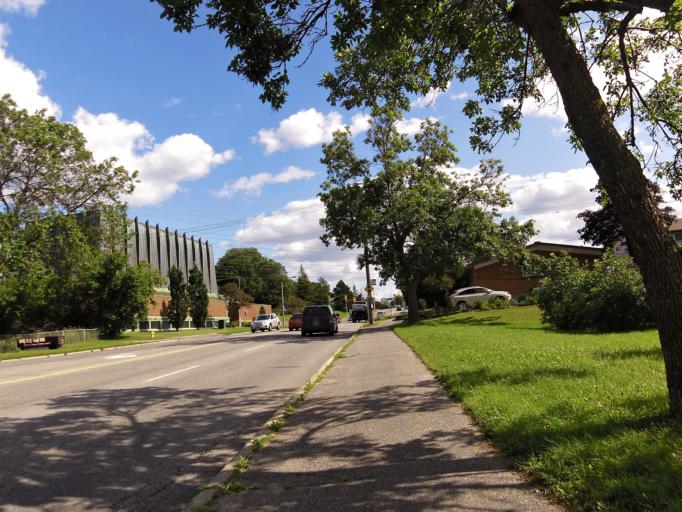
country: CA
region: Ontario
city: Ottawa
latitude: 45.3670
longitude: -75.7521
